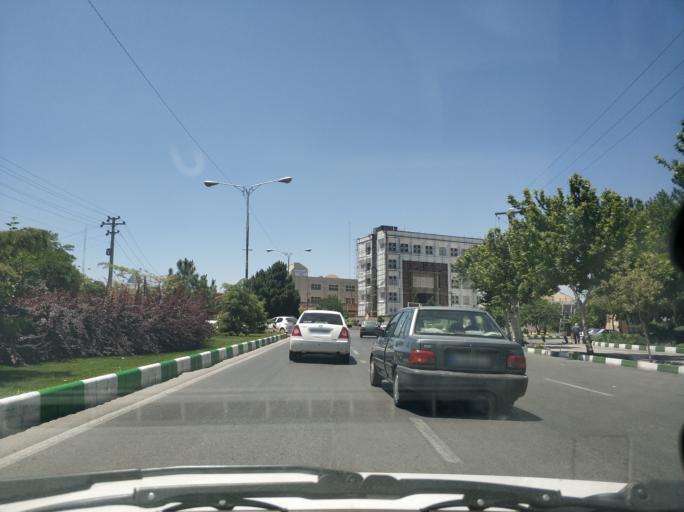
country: IR
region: Razavi Khorasan
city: Mashhad
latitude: 36.3138
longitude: 59.4907
